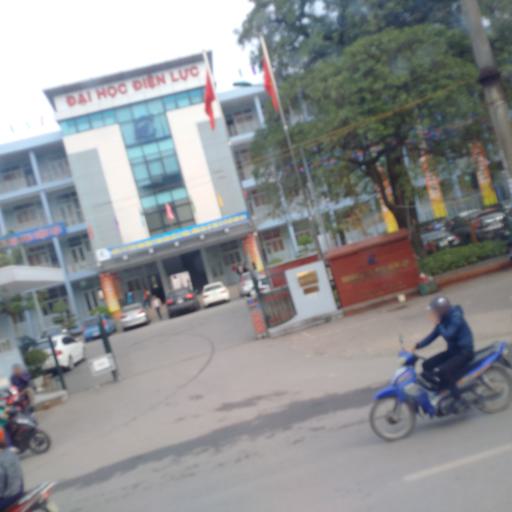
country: VN
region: Ha Noi
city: Cau Giay
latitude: 21.0464
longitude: 105.7864
